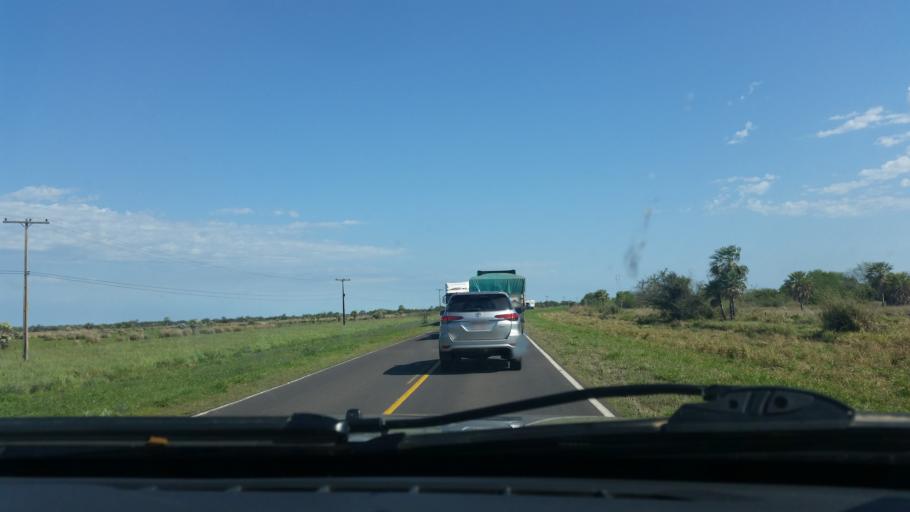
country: PY
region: Presidente Hayes
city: Benjamin Aceval
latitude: -24.6746
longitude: -57.9838
